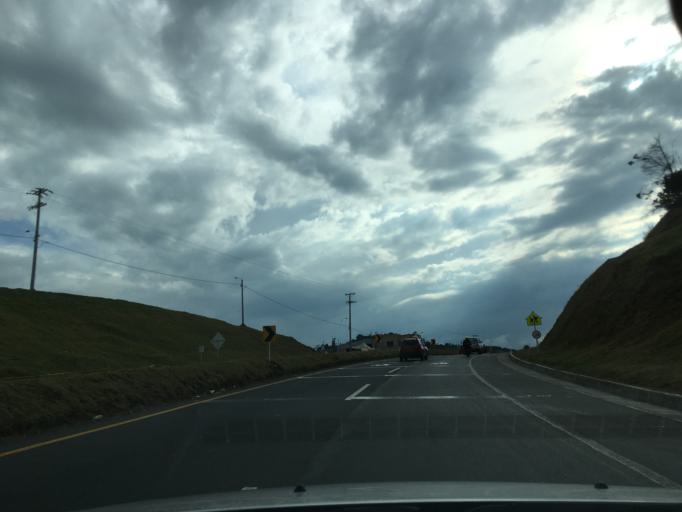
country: CO
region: Boyaca
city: Samaca
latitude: 5.4477
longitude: -73.4330
